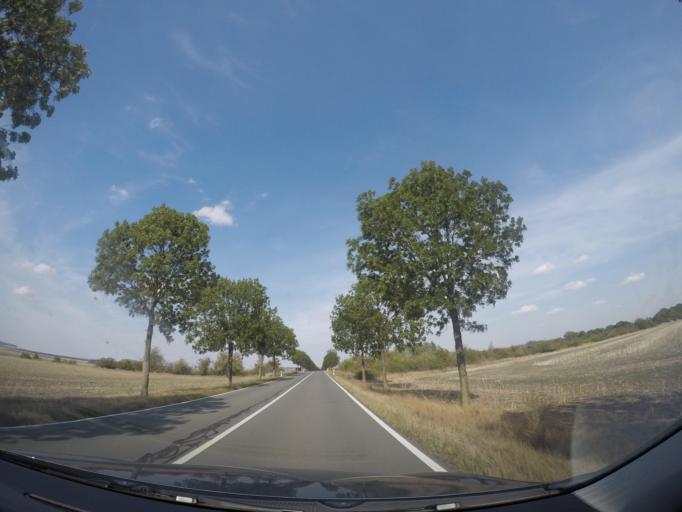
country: DE
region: Saxony-Anhalt
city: Langeln
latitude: 51.9230
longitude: 10.7997
